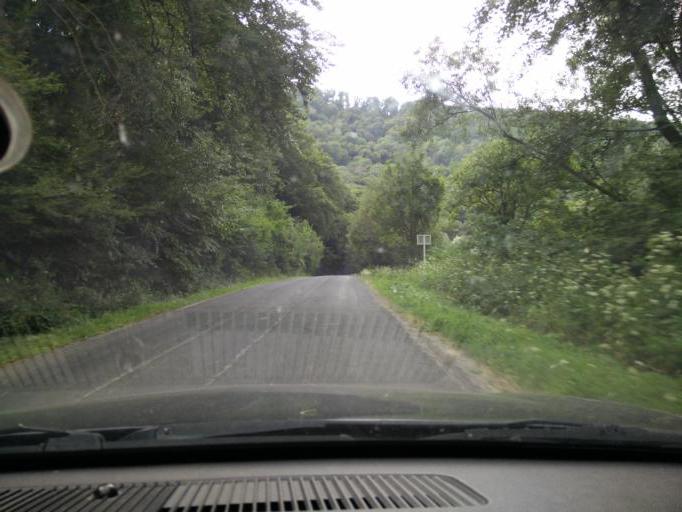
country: HU
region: Komarom-Esztergom
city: Tardos
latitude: 47.6716
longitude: 18.4391
